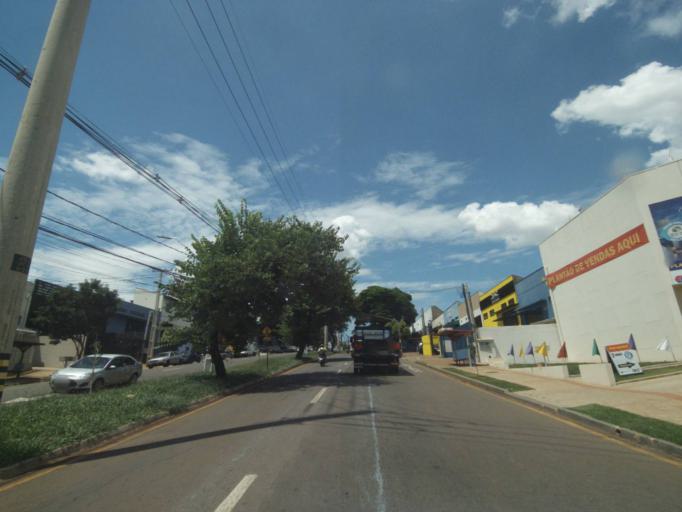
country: BR
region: Parana
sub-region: Londrina
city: Londrina
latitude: -23.3110
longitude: -51.2049
